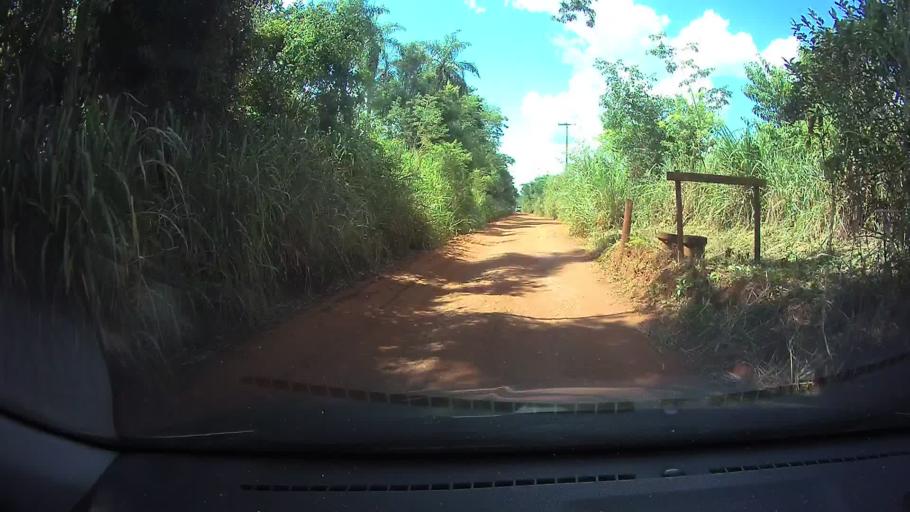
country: PY
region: Paraguari
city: La Colmena
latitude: -25.9073
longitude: -56.7939
